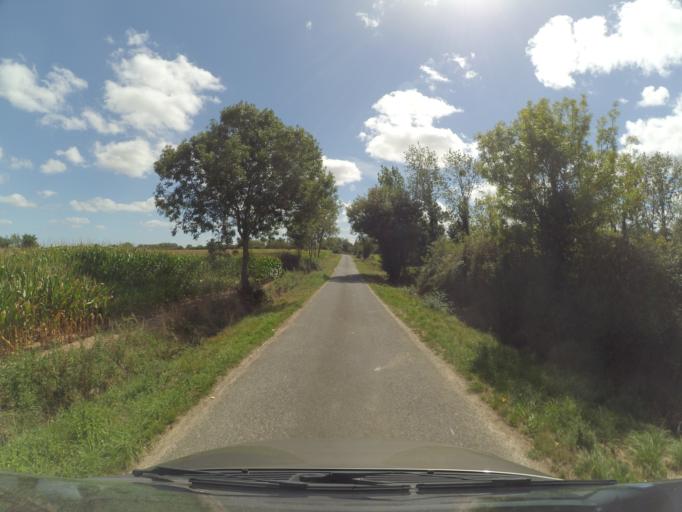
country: FR
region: Pays de la Loire
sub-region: Departement de la Loire-Atlantique
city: Saint-Hilaire-de-Clisson
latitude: 47.0441
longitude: -1.3332
